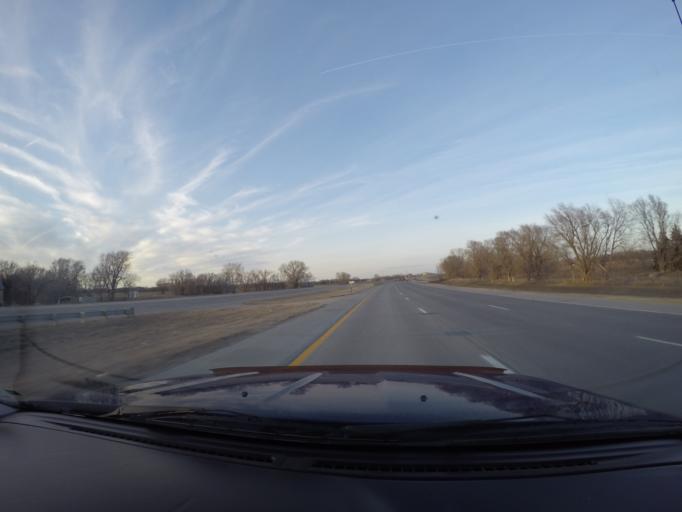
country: US
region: Kansas
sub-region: Saline County
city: Salina
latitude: 38.8448
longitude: -97.6474
